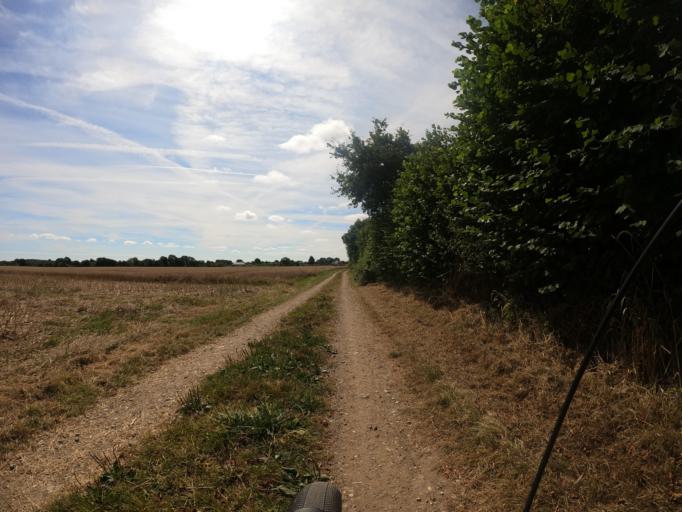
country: DE
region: Schleswig-Holstein
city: Steinbergkirche
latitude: 54.7874
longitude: 9.7544
